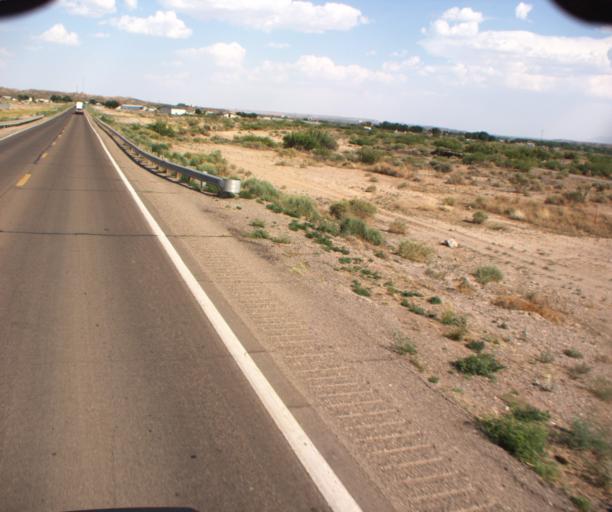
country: US
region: Arizona
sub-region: Greenlee County
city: Clifton
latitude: 32.7451
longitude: -109.1034
